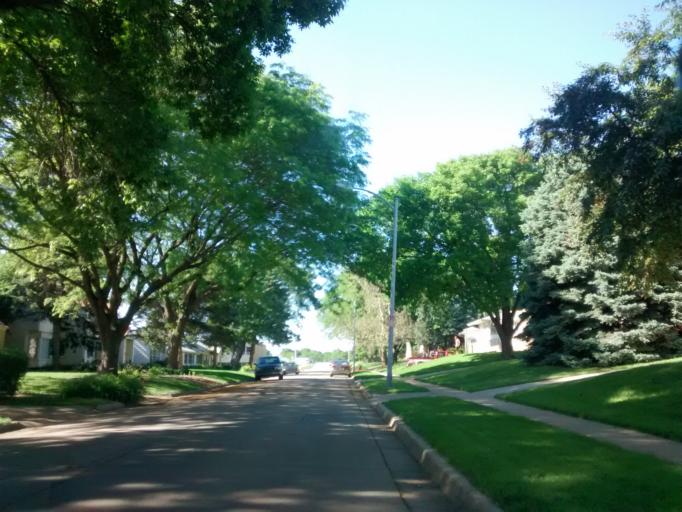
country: US
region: Nebraska
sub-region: Douglas County
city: Ralston
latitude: 41.2580
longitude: -96.0195
